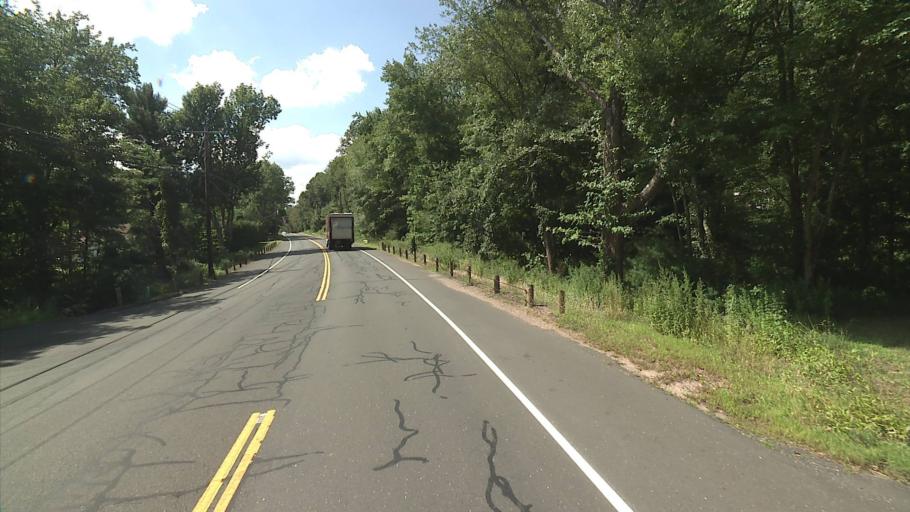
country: US
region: Connecticut
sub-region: Tolland County
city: Somers
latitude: 41.9819
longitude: -72.4112
